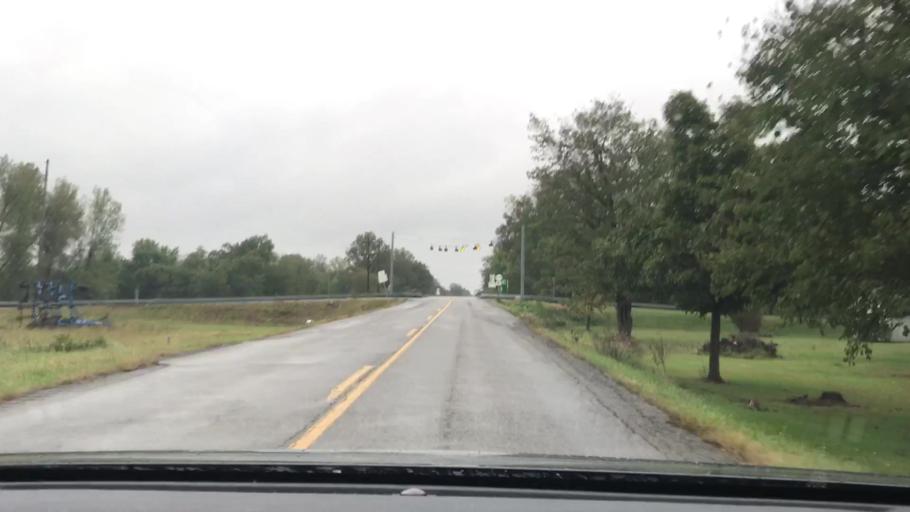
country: US
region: Kentucky
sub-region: McLean County
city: Calhoun
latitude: 37.5262
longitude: -87.3560
